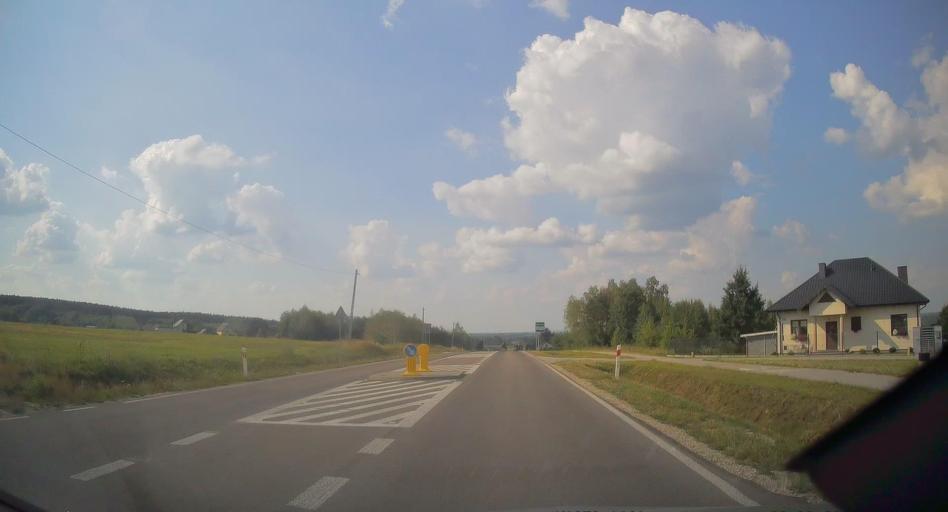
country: PL
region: Swietokrzyskie
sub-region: Powiat konecki
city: Radoszyce
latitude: 51.0353
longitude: 20.2858
